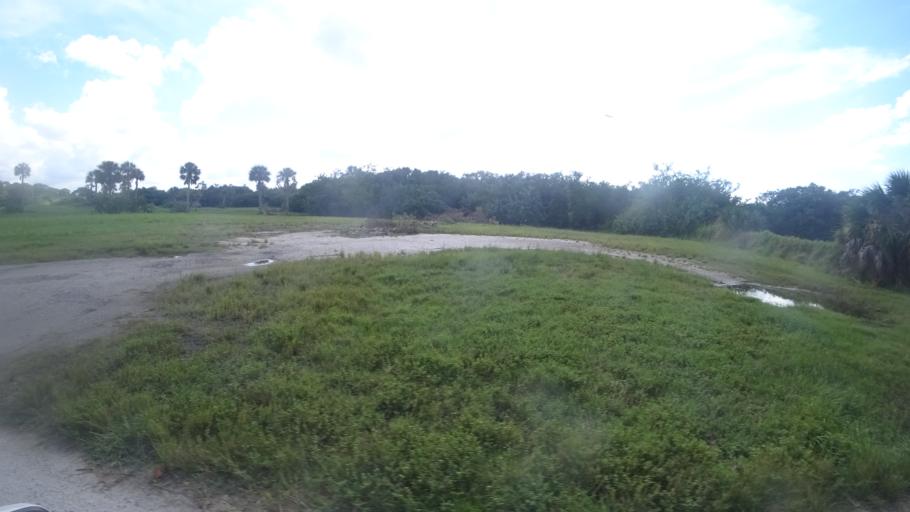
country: US
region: Florida
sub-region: Manatee County
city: Memphis
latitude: 27.6423
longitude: -82.5566
